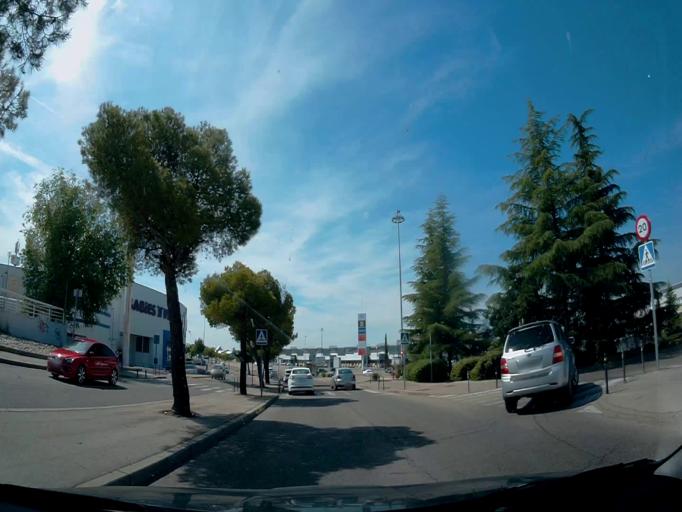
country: ES
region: Madrid
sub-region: Provincia de Madrid
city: Mostoles
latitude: 40.3465
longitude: -3.8525
